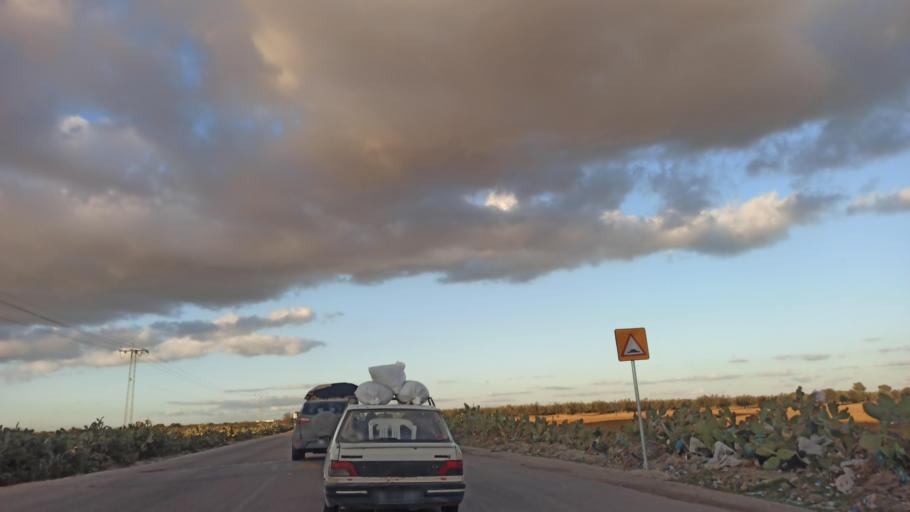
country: TN
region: Susah
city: Sidi Bou Ali
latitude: 36.0126
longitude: 10.3184
